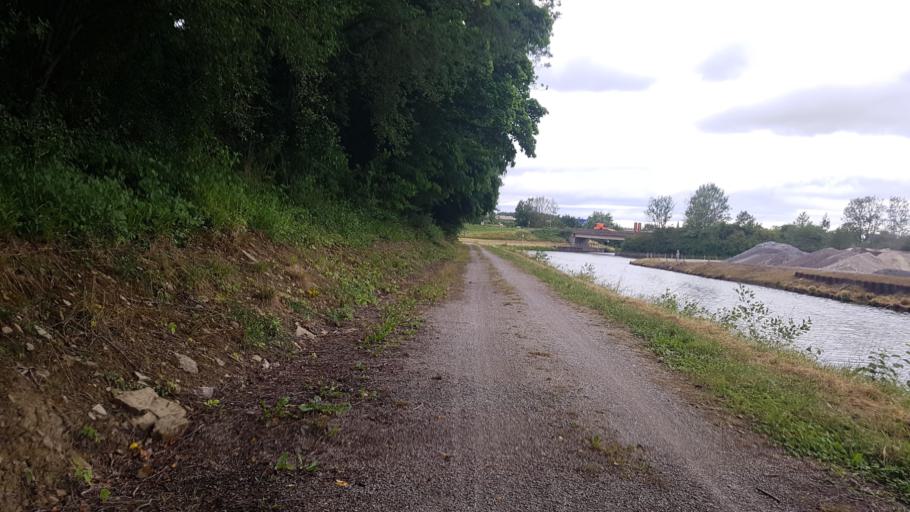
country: FR
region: Lorraine
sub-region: Departement de la Moselle
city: Lorquin
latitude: 48.6882
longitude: 6.9623
